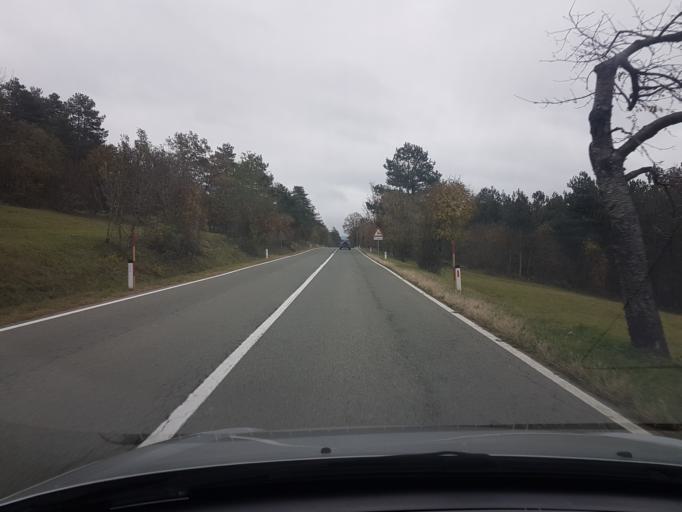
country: SI
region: Divaca
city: Divaca
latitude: 45.7314
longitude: 13.9601
